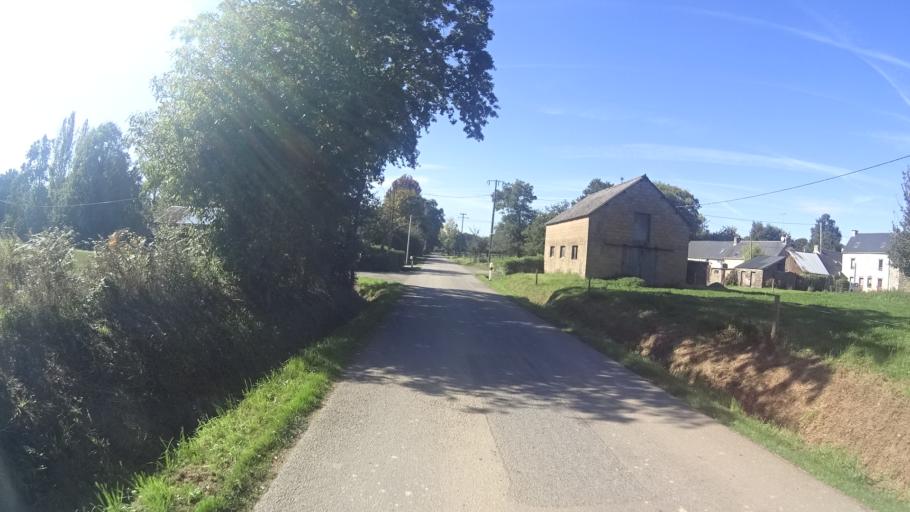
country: FR
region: Brittany
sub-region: Departement du Morbihan
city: Peillac
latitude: 47.7320
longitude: -2.1812
